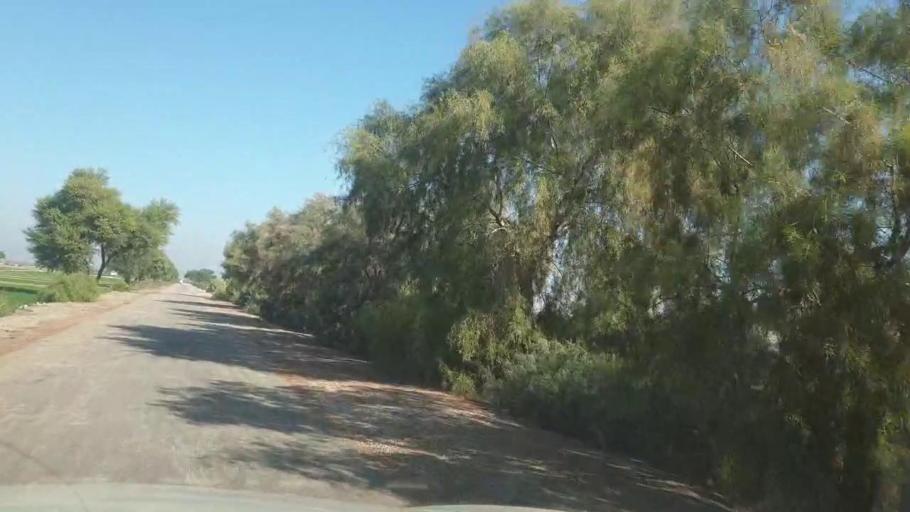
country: PK
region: Sindh
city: Bhan
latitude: 26.5350
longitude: 67.6448
